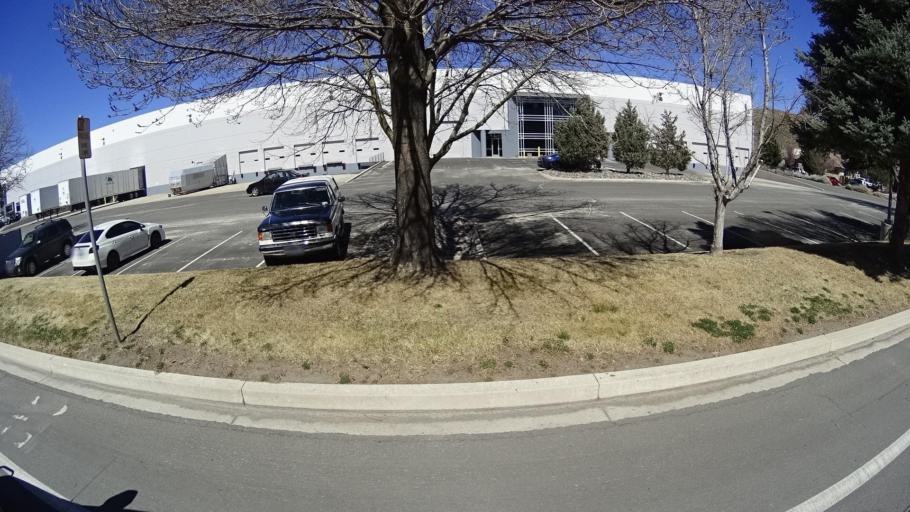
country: US
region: Nevada
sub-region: Washoe County
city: Sparks
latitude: 39.4611
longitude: -119.7683
